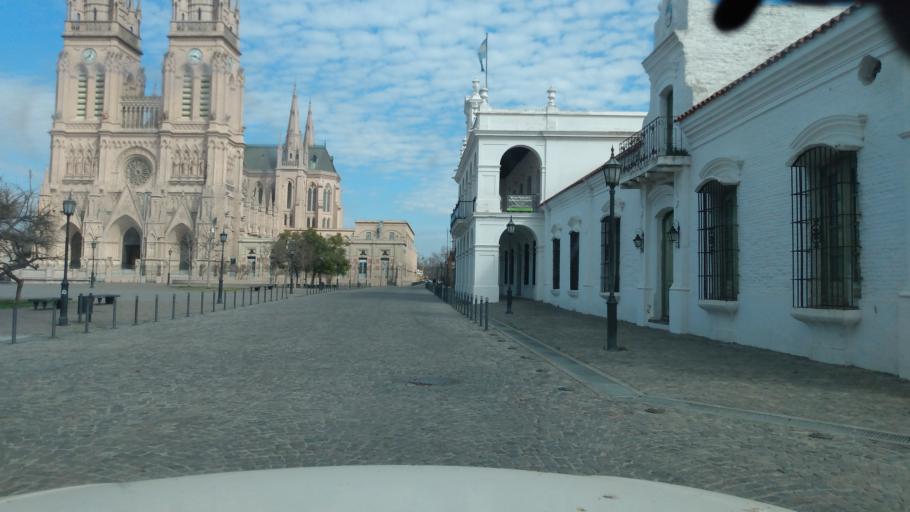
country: AR
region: Buenos Aires
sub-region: Partido de Lujan
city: Lujan
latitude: -34.5626
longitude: -59.1215
